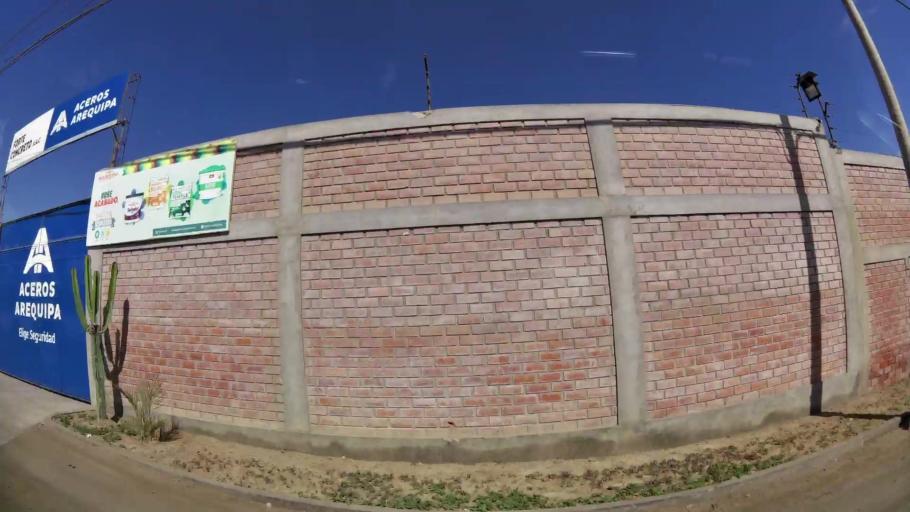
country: PE
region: Ica
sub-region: Provincia de Chincha
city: Sunampe
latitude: -13.4175
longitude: -76.1580
